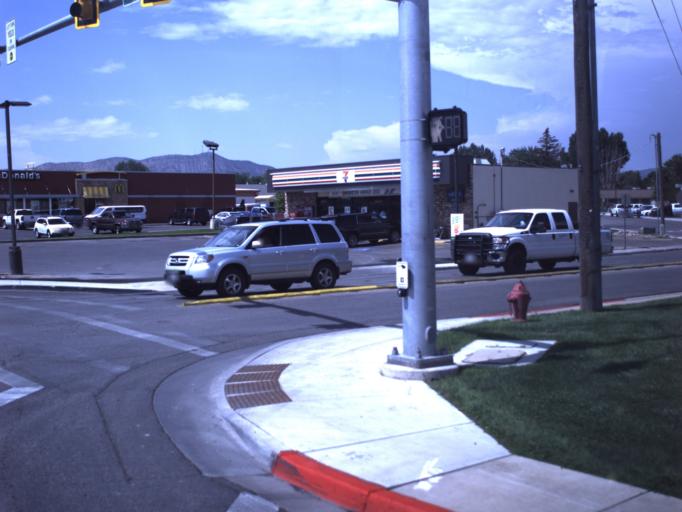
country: US
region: Utah
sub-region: Uintah County
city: Vernal
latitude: 40.4543
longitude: -109.5453
